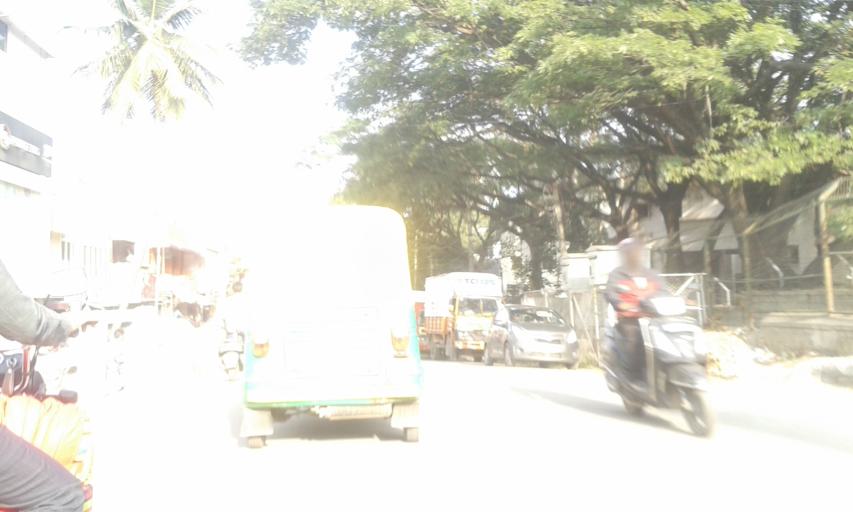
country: IN
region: Karnataka
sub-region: Bangalore Urban
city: Bangalore
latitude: 12.9708
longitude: 77.6339
